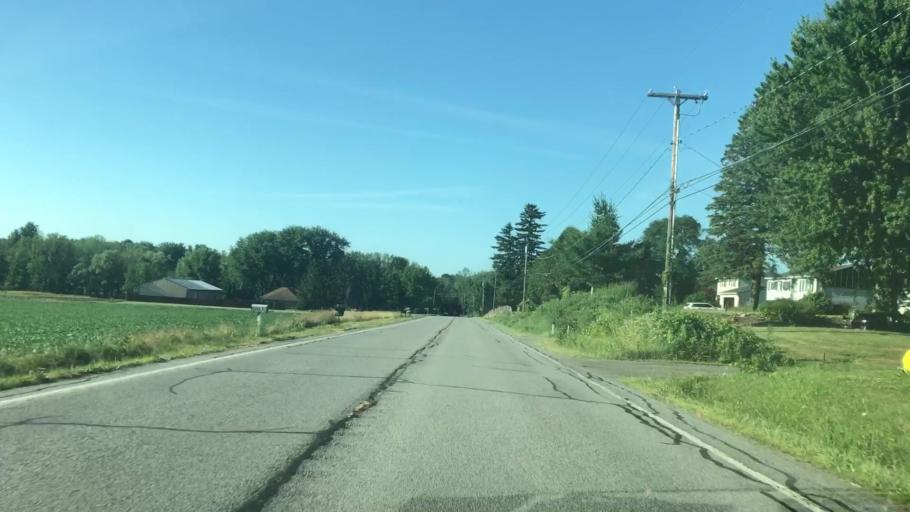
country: US
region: New York
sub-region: Wayne County
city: Ontario
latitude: 43.1608
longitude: -77.2905
